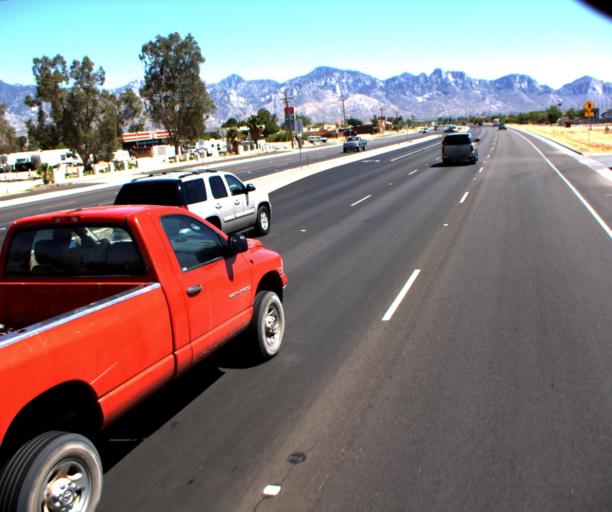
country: US
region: Arizona
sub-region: Pima County
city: Catalina
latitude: 32.4990
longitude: -110.9263
